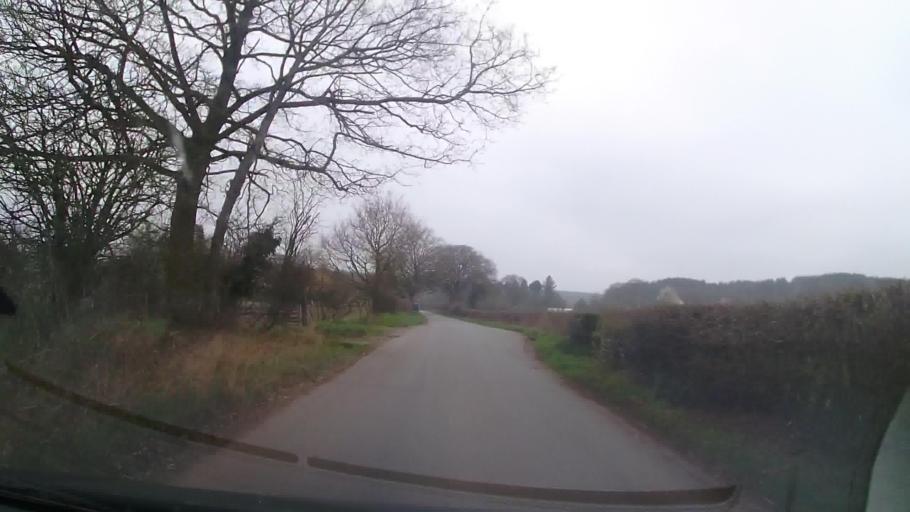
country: GB
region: England
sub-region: Staffordshire
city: Standon
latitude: 52.9455
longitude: -2.3519
